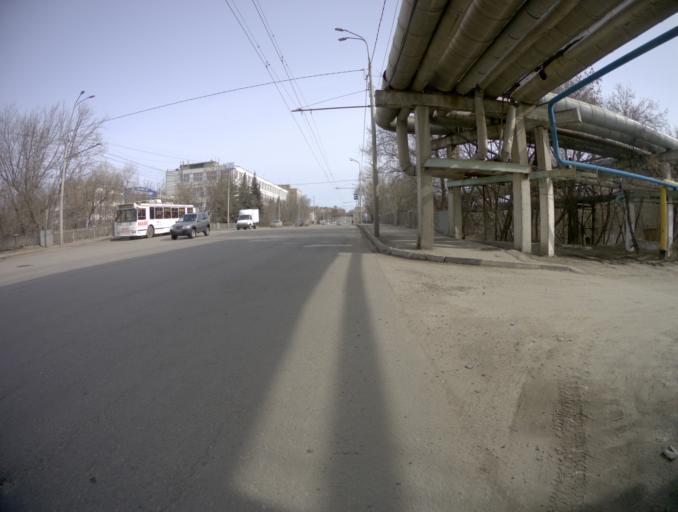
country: RU
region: Vladimir
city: Kommunar
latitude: 56.1457
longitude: 40.4446
